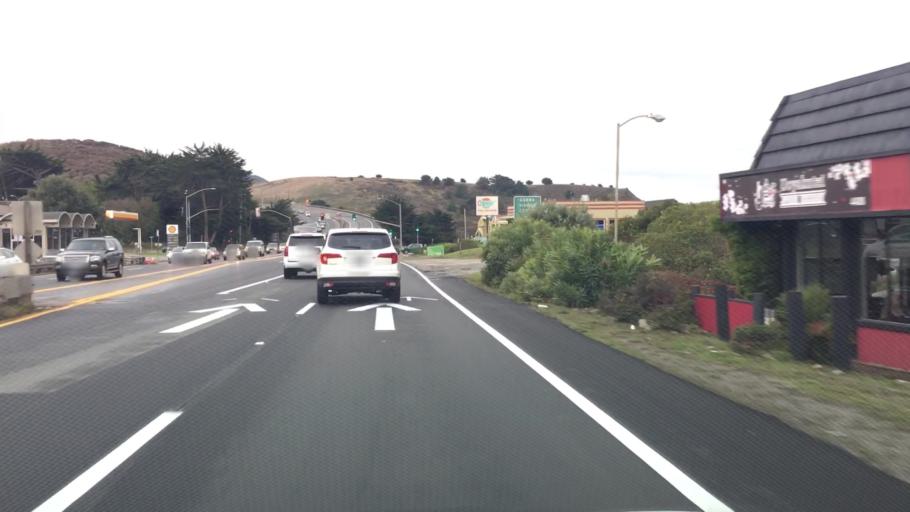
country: US
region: California
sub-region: San Mateo County
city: Pacifica
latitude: 37.6089
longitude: -122.4933
